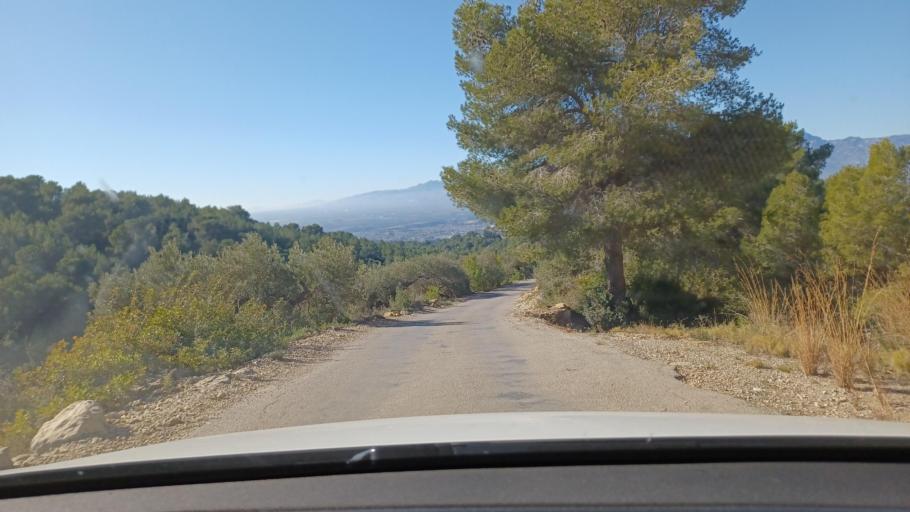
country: ES
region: Catalonia
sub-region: Provincia de Tarragona
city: Tortosa
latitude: 40.8159
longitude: 0.5629
